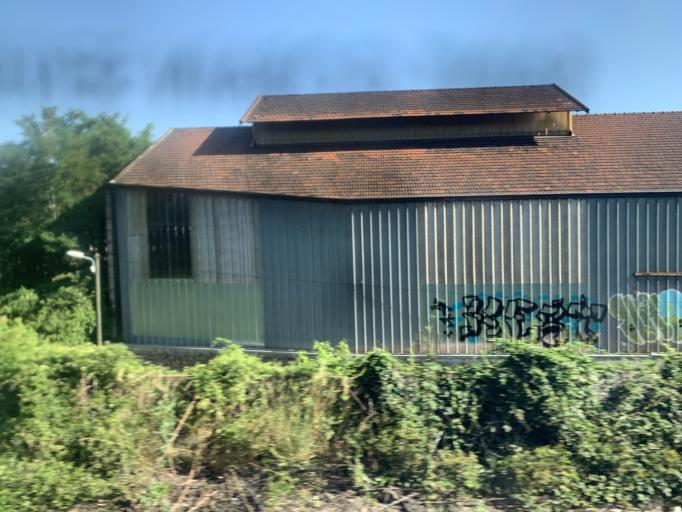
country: FR
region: Rhone-Alpes
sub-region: Departement de la Loire
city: Lorette
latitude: 45.5142
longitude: 4.5794
